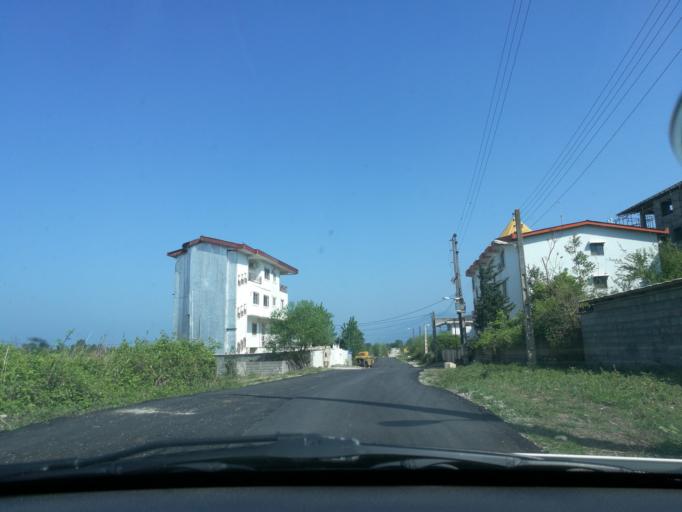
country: IR
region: Mazandaran
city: Chalus
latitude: 36.6726
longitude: 51.4315
